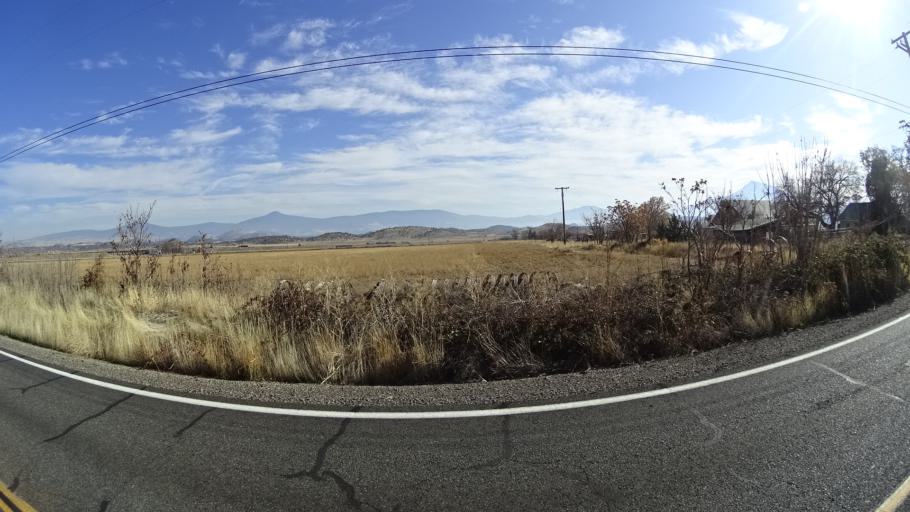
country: US
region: California
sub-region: Siskiyou County
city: Montague
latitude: 41.6219
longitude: -122.5298
